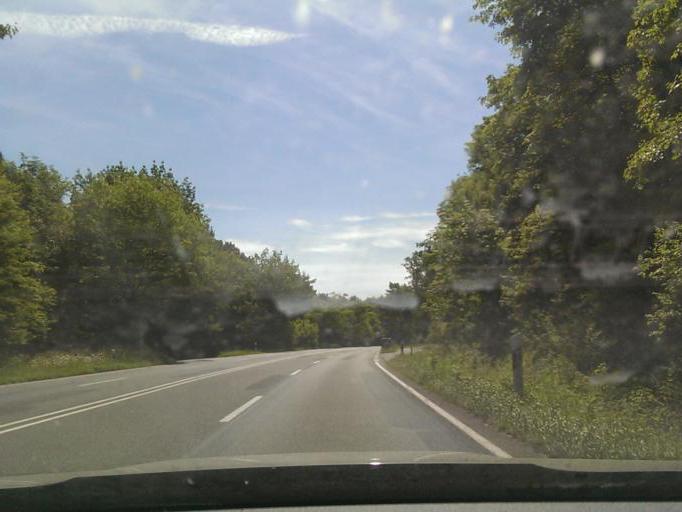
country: DE
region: Lower Saxony
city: Alfeld
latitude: 51.9813
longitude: 9.8100
